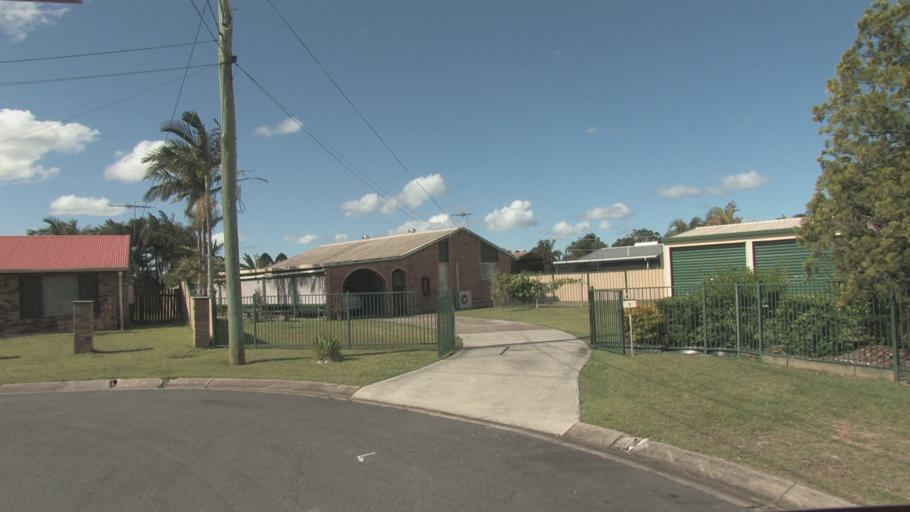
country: AU
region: Queensland
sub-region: Logan
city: Waterford West
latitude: -27.6814
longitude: 153.1520
